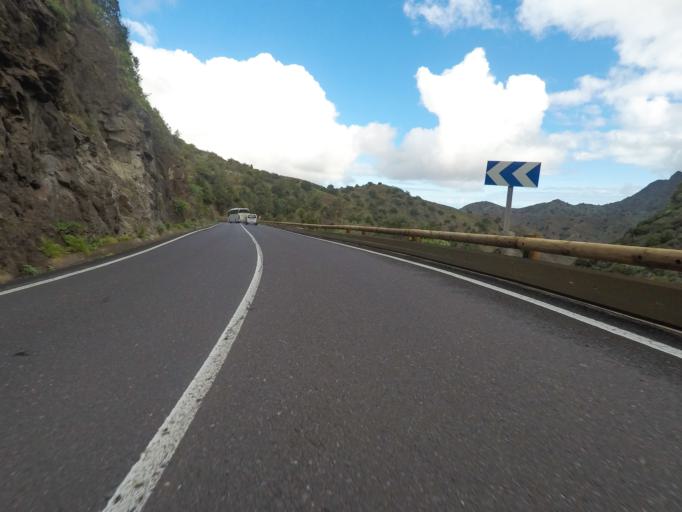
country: ES
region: Canary Islands
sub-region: Provincia de Santa Cruz de Tenerife
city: Hermigua
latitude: 28.1366
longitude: -17.2008
